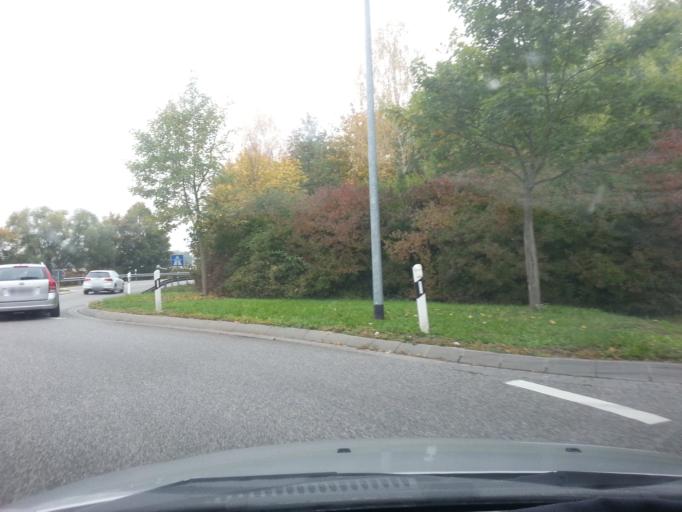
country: DE
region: Rheinland-Pfalz
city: Lachen-Speyerdorf
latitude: 49.3253
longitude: 8.1799
